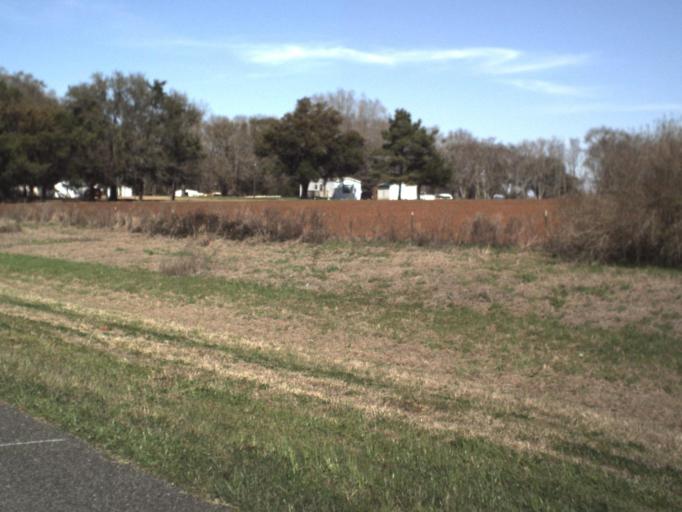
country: US
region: Florida
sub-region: Jackson County
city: Graceville
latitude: 30.9172
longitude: -85.3811
